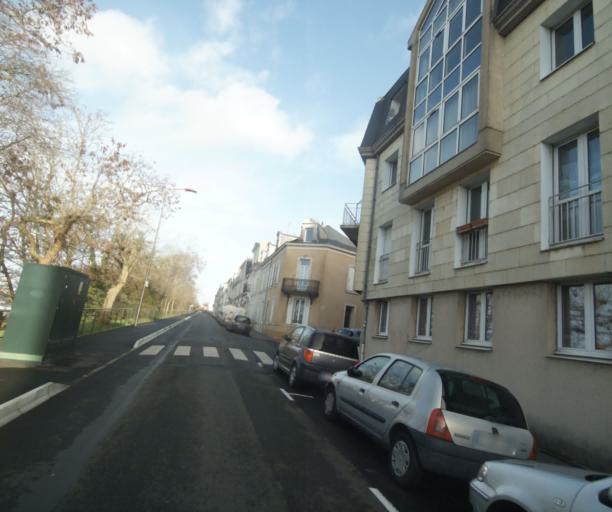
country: FR
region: Pays de la Loire
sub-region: Departement de la Sarthe
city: Le Mans
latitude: 47.9987
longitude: 0.1894
